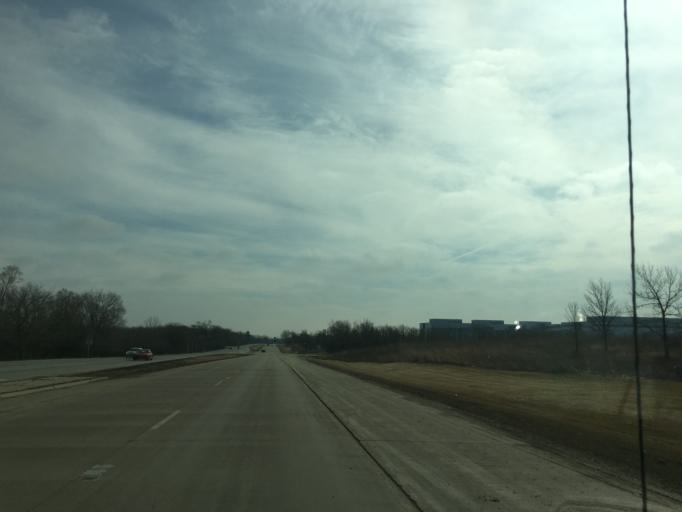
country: US
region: Illinois
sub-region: Kane County
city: East Dundee
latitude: 42.0811
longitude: -88.2231
